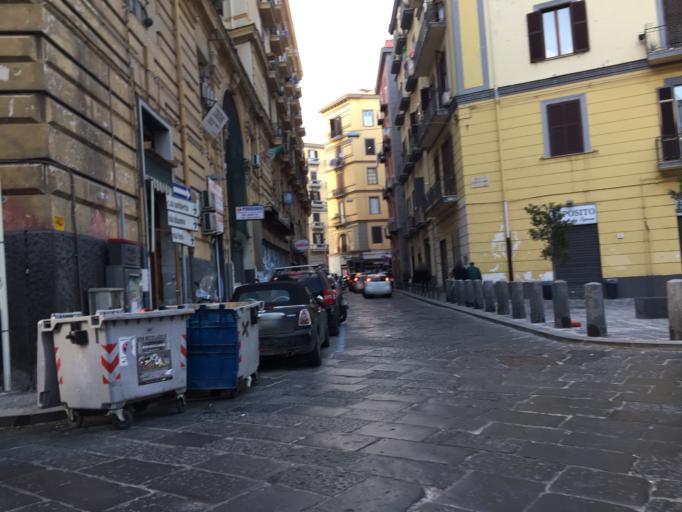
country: IT
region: Campania
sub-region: Provincia di Napoli
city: Napoli
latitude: 40.8472
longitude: 14.2626
